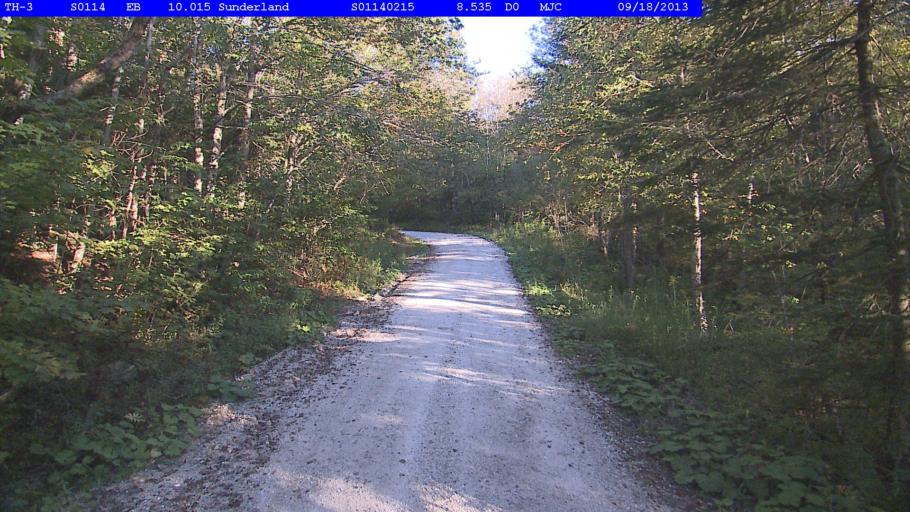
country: US
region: Vermont
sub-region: Bennington County
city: Manchester Center
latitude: 43.0542
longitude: -73.0224
